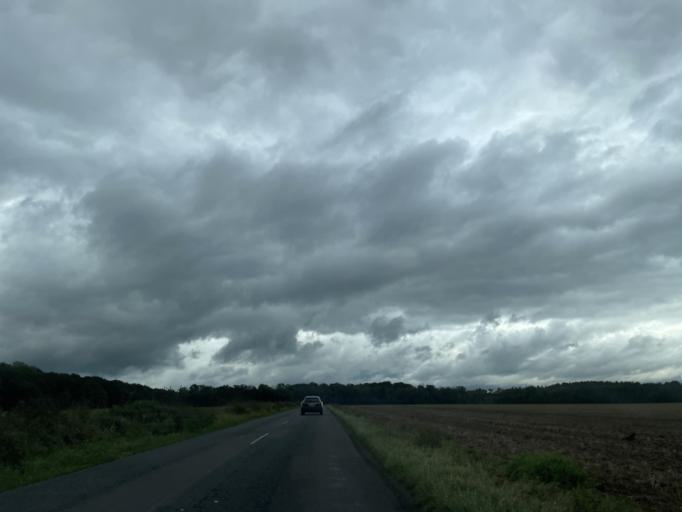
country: FR
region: Ile-de-France
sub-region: Departement de Seine-et-Marne
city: Sammeron
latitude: 48.8876
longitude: 3.0675
